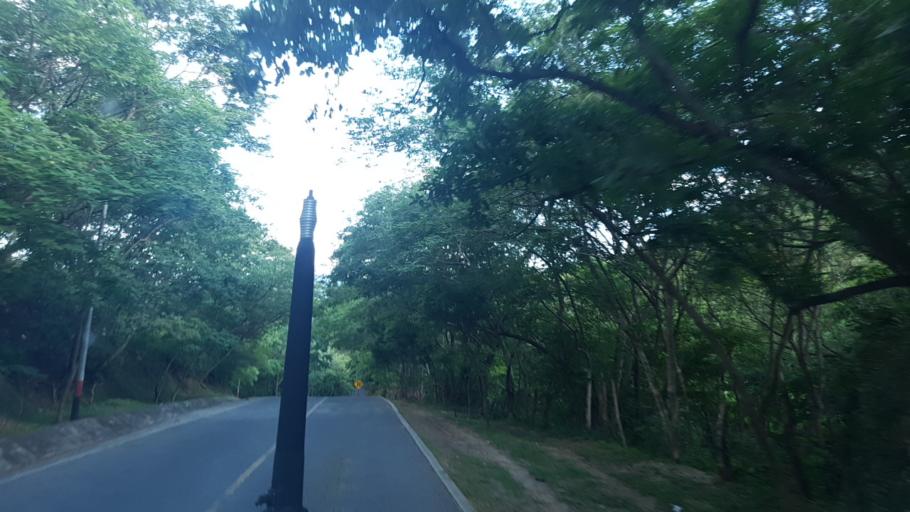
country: NI
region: Nueva Segovia
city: Ocotal
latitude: 13.6492
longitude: -86.6089
